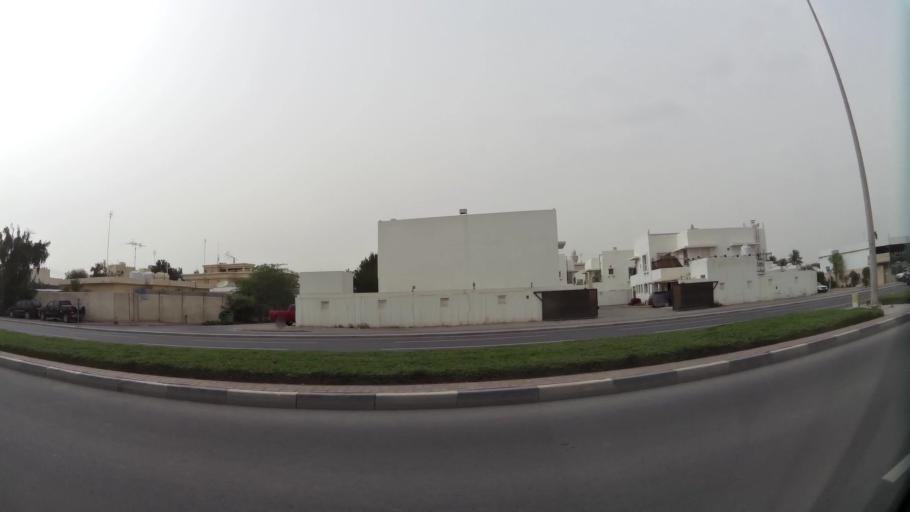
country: QA
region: Baladiyat ad Dawhah
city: Doha
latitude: 25.2567
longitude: 51.4953
